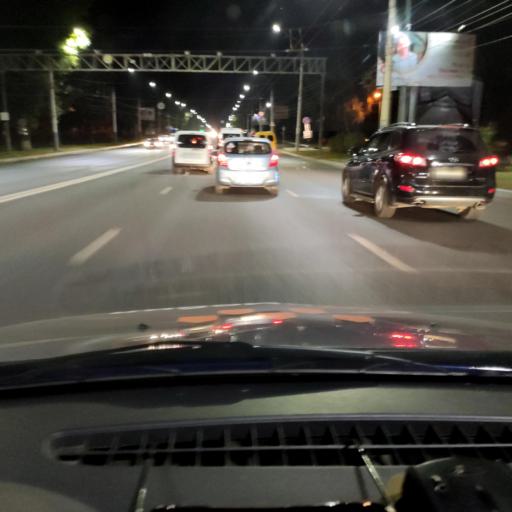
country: RU
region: Voronezj
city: Voronezh
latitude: 51.6590
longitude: 39.2456
